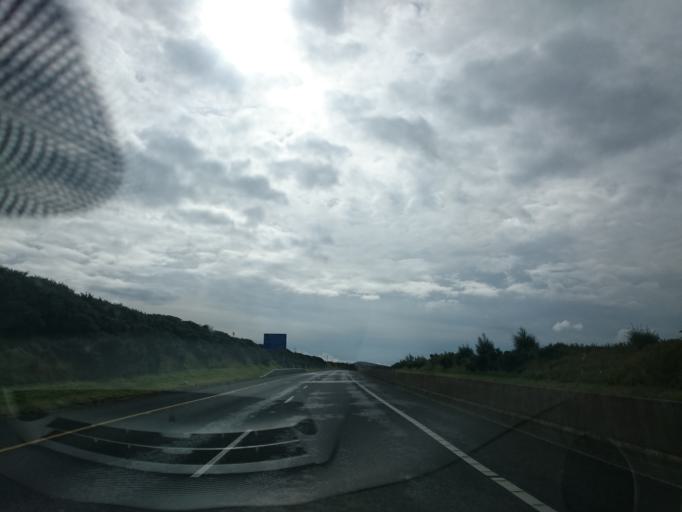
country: IE
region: Leinster
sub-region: Kilkenny
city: Mooncoin
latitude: 52.3964
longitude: -7.1758
